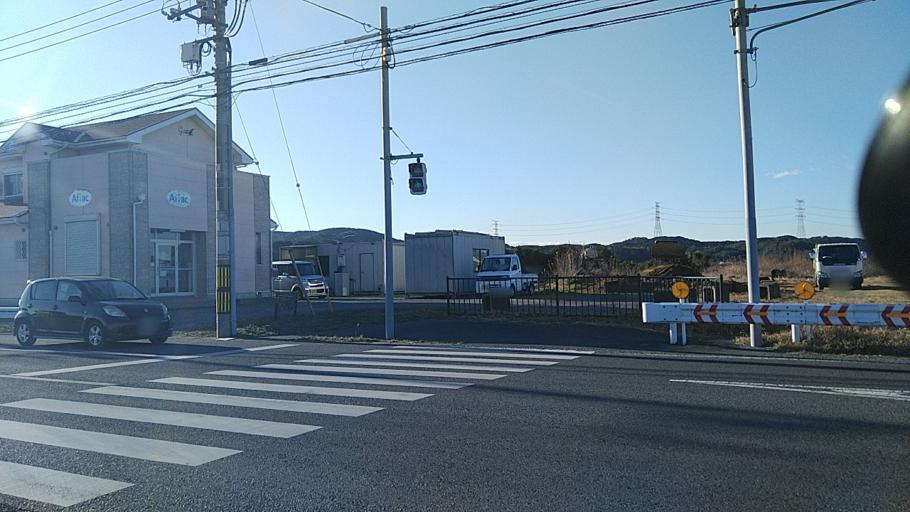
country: JP
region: Chiba
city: Kimitsu
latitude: 35.3205
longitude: 139.8836
